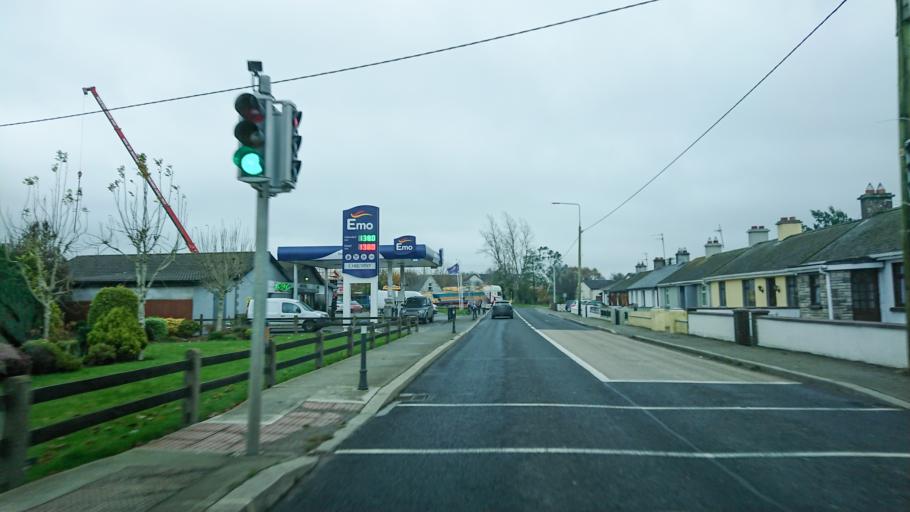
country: IE
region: Leinster
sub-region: Kilkenny
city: Mooncoin
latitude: 52.2919
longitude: -7.2531
